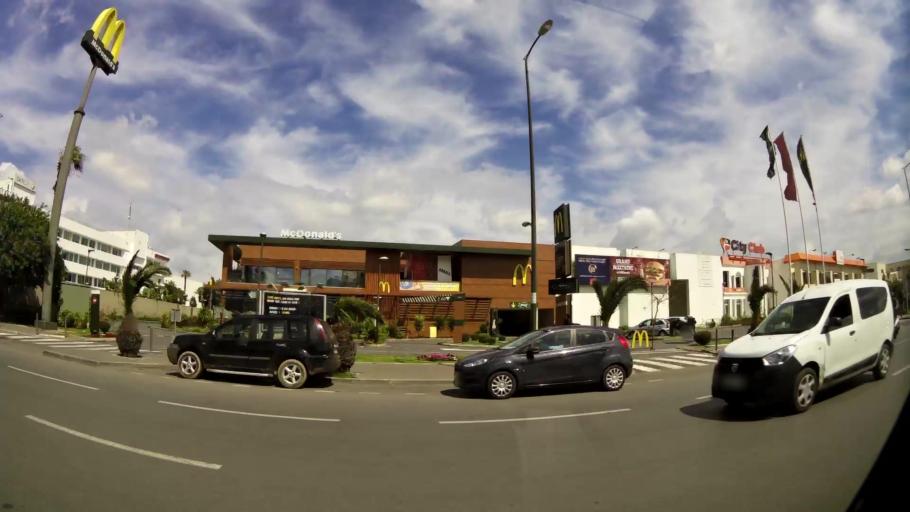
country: MA
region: Grand Casablanca
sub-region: Casablanca
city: Casablanca
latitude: 33.6033
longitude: -7.5490
